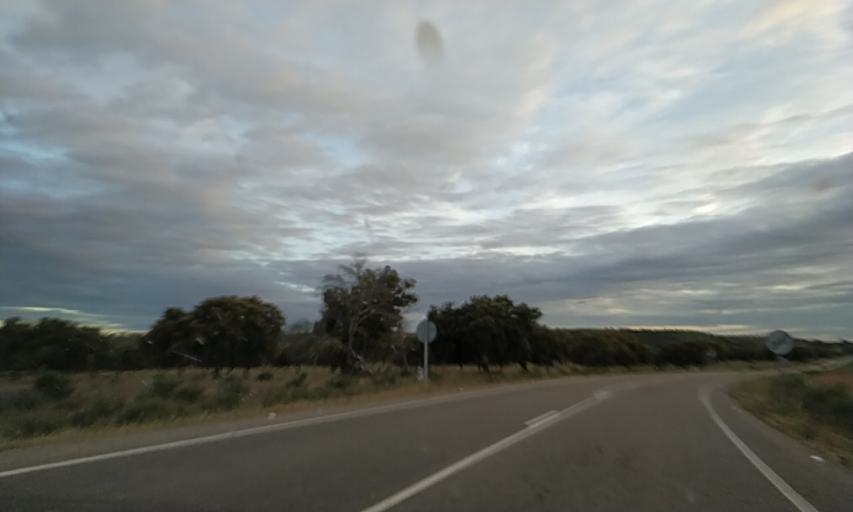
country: ES
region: Extremadura
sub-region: Provincia de Badajoz
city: La Roca de la Sierra
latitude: 39.0967
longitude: -6.7133
